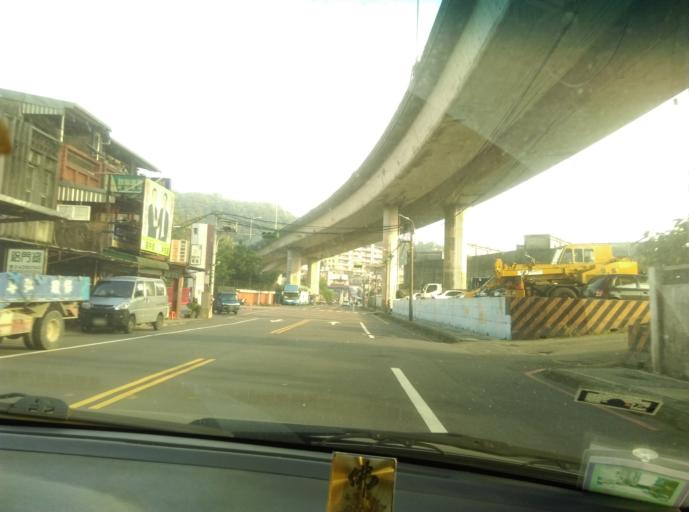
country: TW
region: Taiwan
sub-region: Keelung
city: Keelung
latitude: 25.1535
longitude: 121.7344
